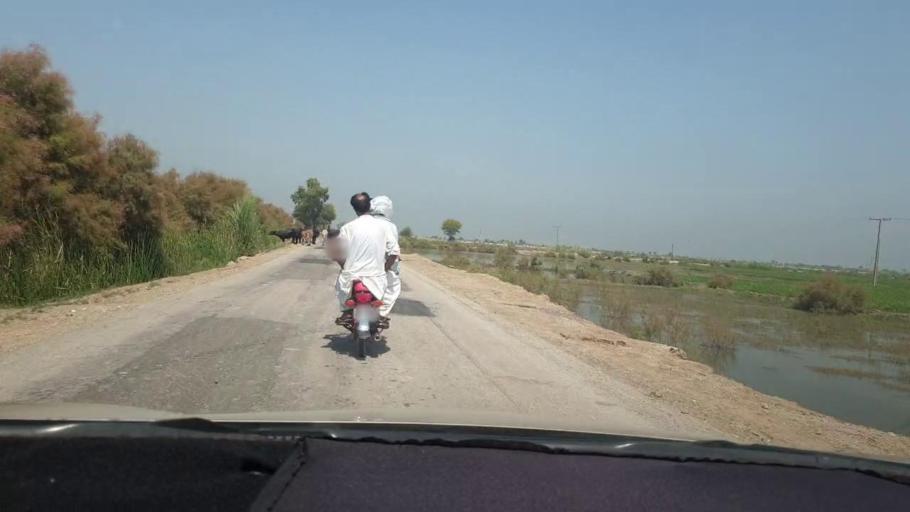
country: PK
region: Sindh
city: Shahdadkot
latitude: 27.8389
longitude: 68.0085
